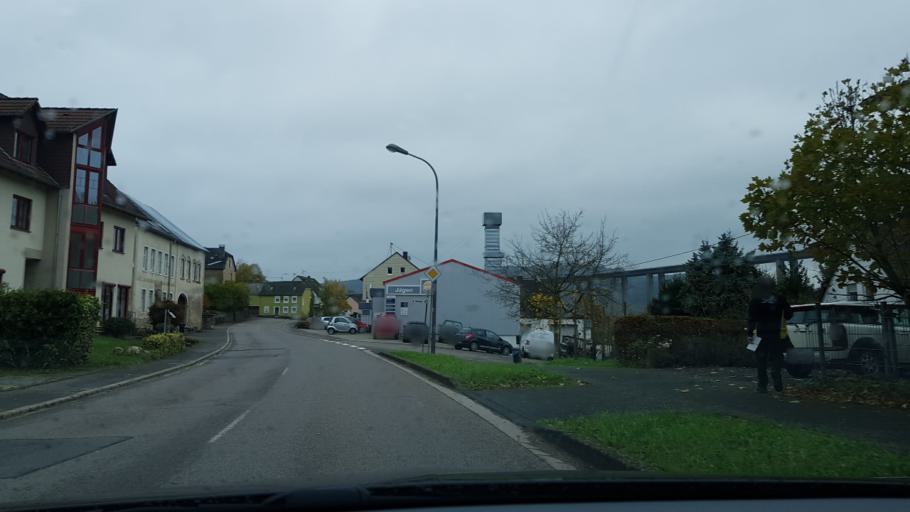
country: DE
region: Rheinland-Pfalz
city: Longuich
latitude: 49.7886
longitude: 6.7727
